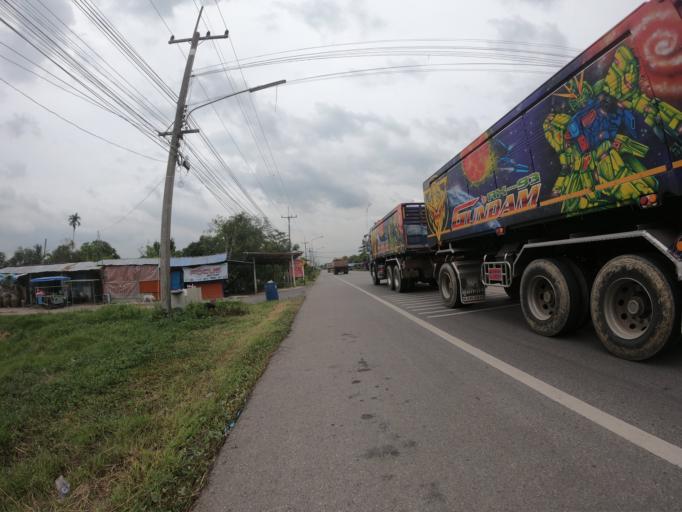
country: TH
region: Pathum Thani
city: Nong Suea
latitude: 14.0512
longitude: 100.8709
